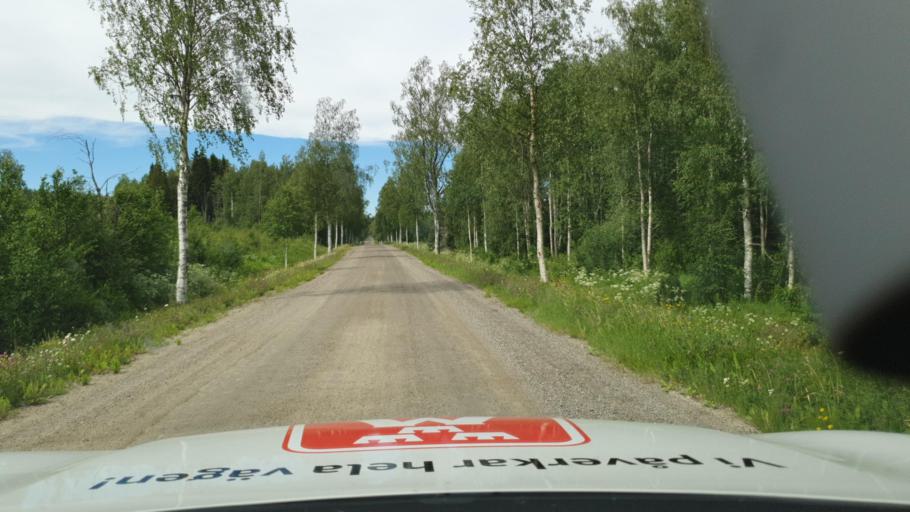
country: SE
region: Vaesterbotten
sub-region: Skelleftea Kommun
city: Burtraesk
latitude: 64.4688
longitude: 20.4588
